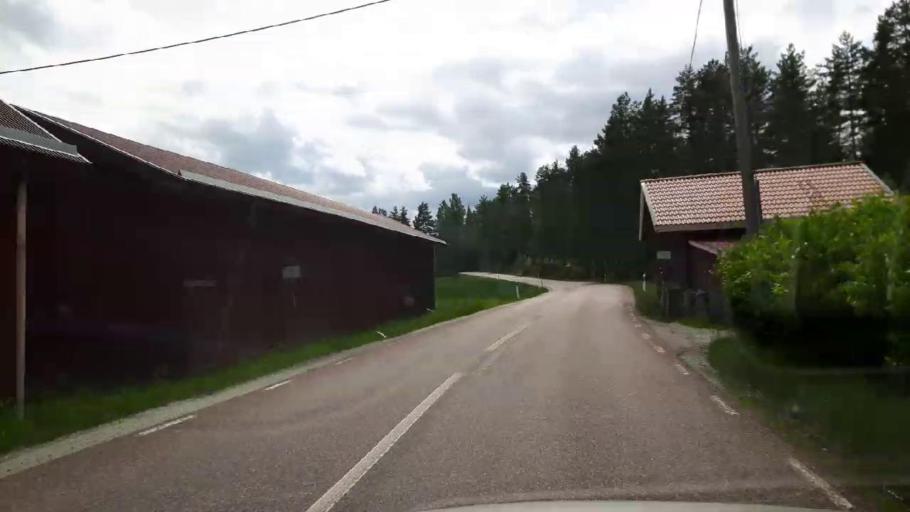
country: SE
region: Vaestmanland
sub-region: Fagersta Kommun
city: Fagersta
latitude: 59.9128
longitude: 15.8244
